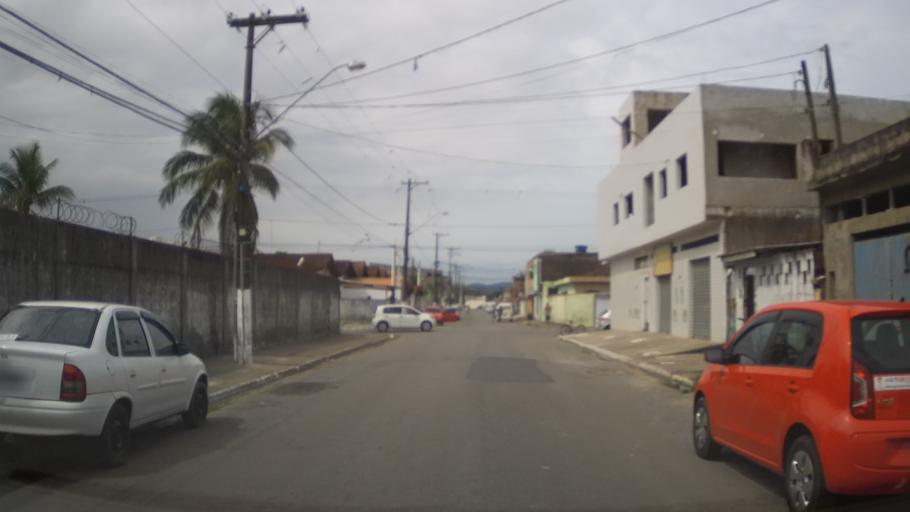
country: BR
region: Sao Paulo
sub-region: Praia Grande
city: Praia Grande
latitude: -24.0002
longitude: -46.4501
